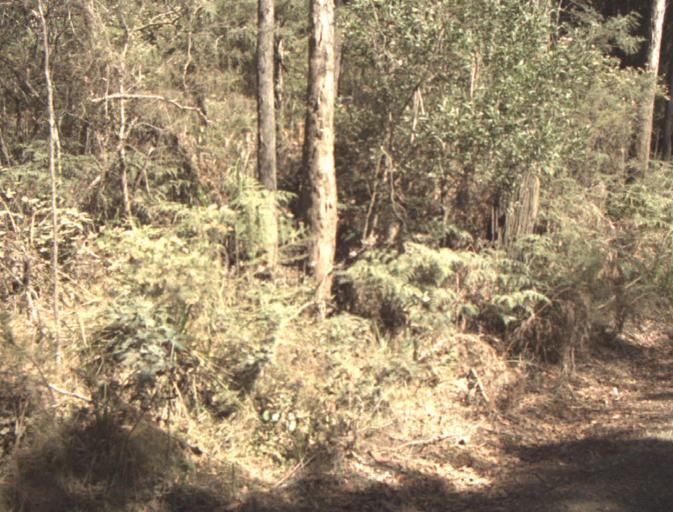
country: AU
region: Tasmania
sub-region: Launceston
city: Newstead
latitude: -41.3780
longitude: 147.2880
